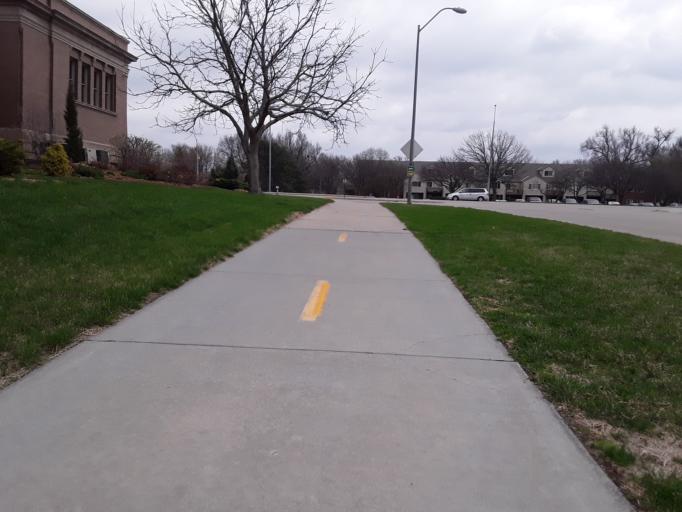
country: US
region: Nebraska
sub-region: Lancaster County
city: Lincoln
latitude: 40.8336
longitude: -96.6830
